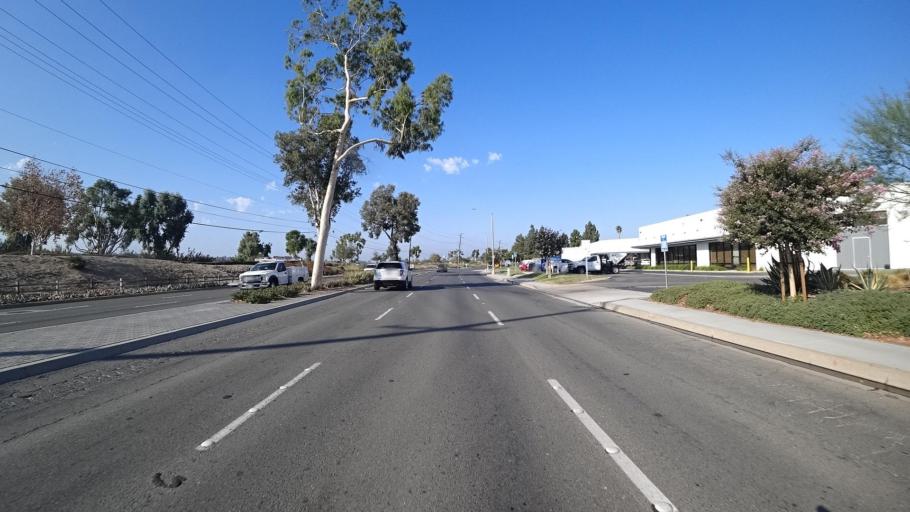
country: US
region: California
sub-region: Orange County
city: Yorba Linda
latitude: 33.8571
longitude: -117.8326
